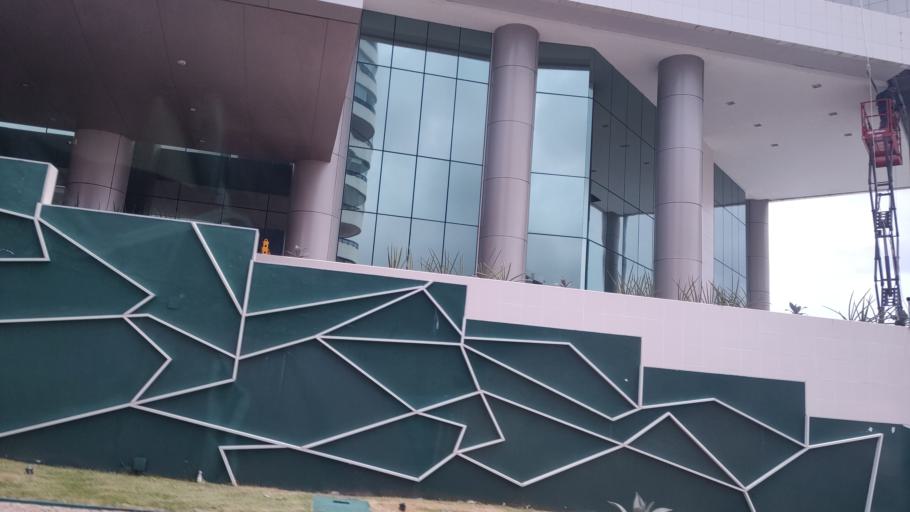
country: BR
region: Maranhao
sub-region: Sao Luis
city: Sao Luis
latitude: -2.4879
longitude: -44.2977
